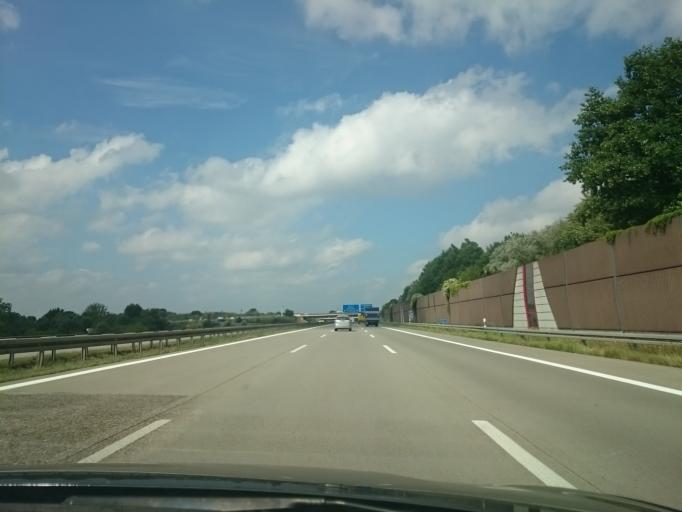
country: DE
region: Brandenburg
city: Ahrensfelde
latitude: 52.5983
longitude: 13.6107
